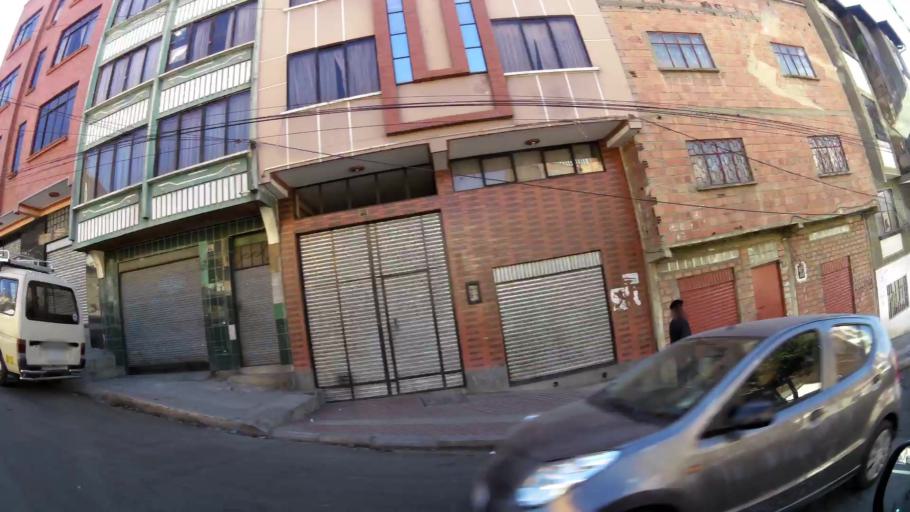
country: BO
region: La Paz
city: La Paz
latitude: -16.5051
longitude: -68.1472
